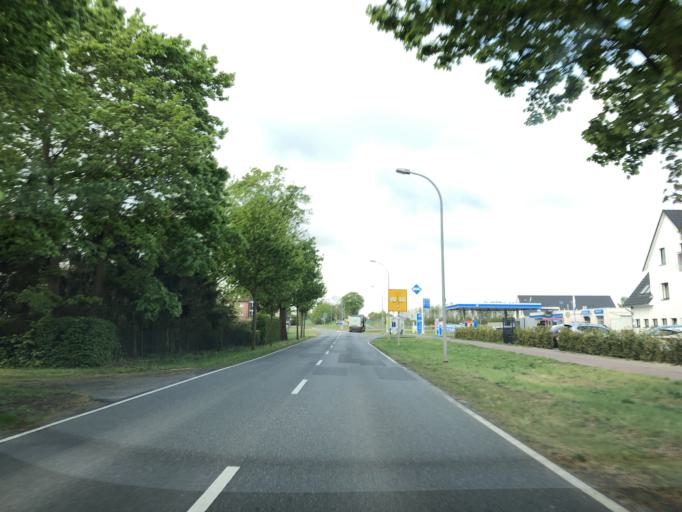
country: DE
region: Mecklenburg-Vorpommern
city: Guestrow
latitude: 53.7733
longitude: 12.1679
